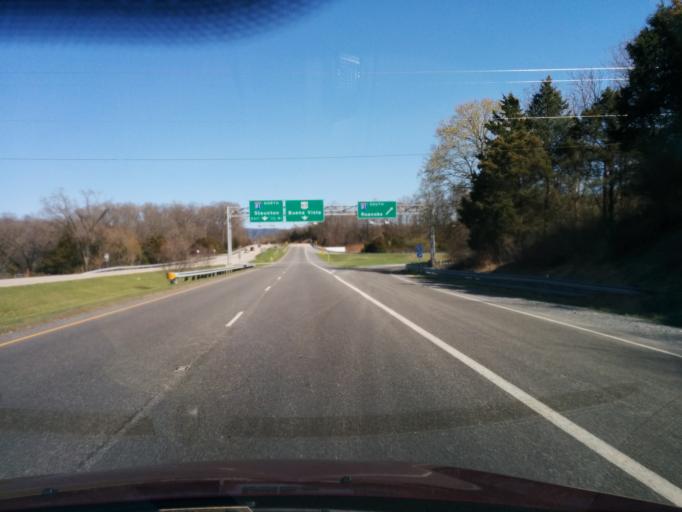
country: US
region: Virginia
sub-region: Rockbridge County
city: East Lexington
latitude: 37.7577
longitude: -79.4137
